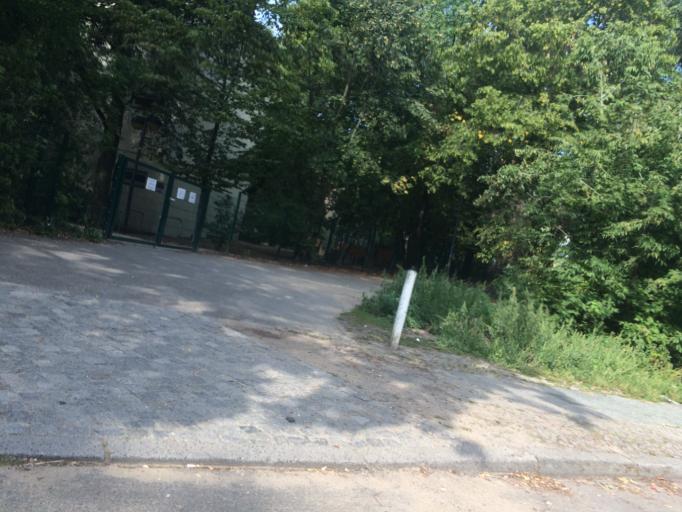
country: DE
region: Berlin
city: Wedding Bezirk
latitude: 52.5571
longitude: 13.3577
